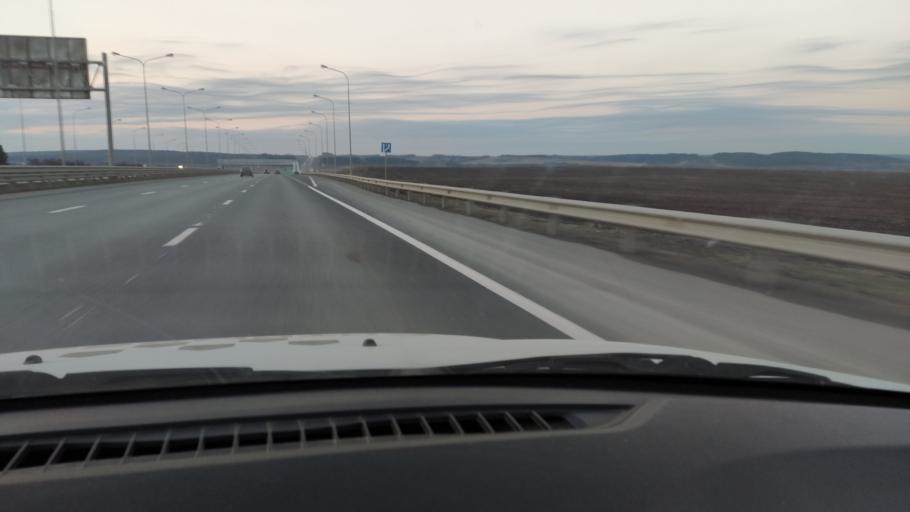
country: RU
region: Perm
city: Zvezdnyy
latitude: 57.7944
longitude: 56.3327
